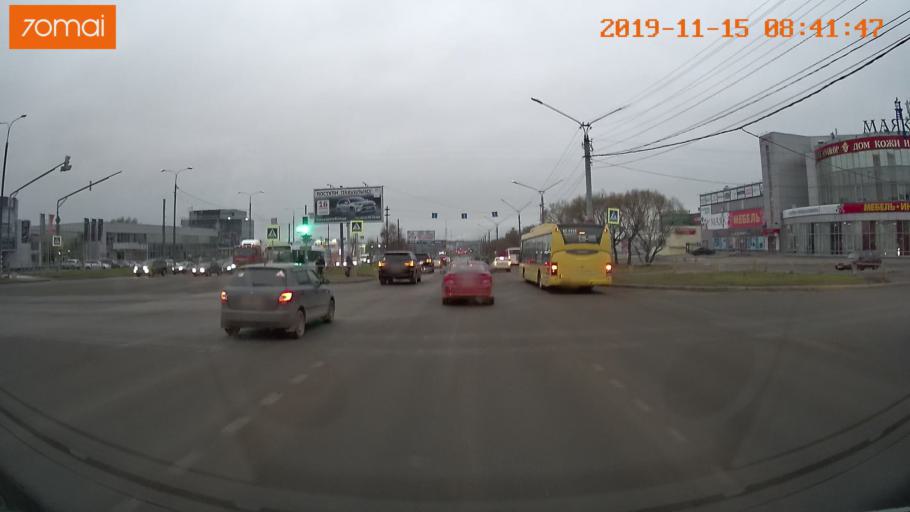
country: RU
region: Vologda
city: Cherepovets
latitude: 59.0982
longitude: 37.9116
